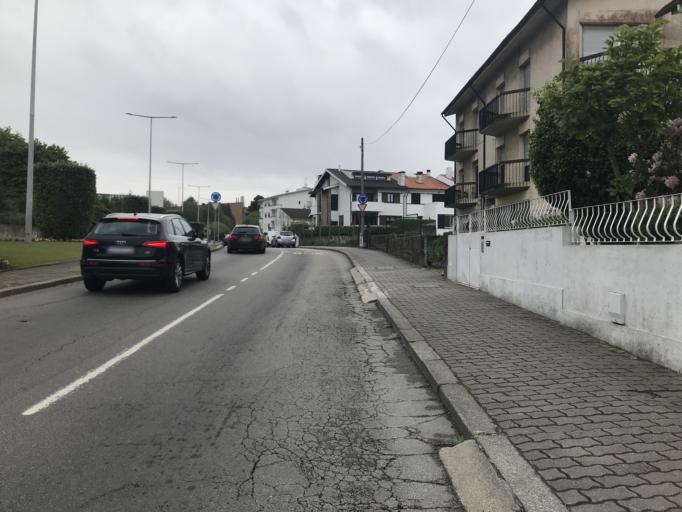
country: PT
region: Porto
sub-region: Matosinhos
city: Senhora da Hora
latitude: 41.1802
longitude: -8.6622
